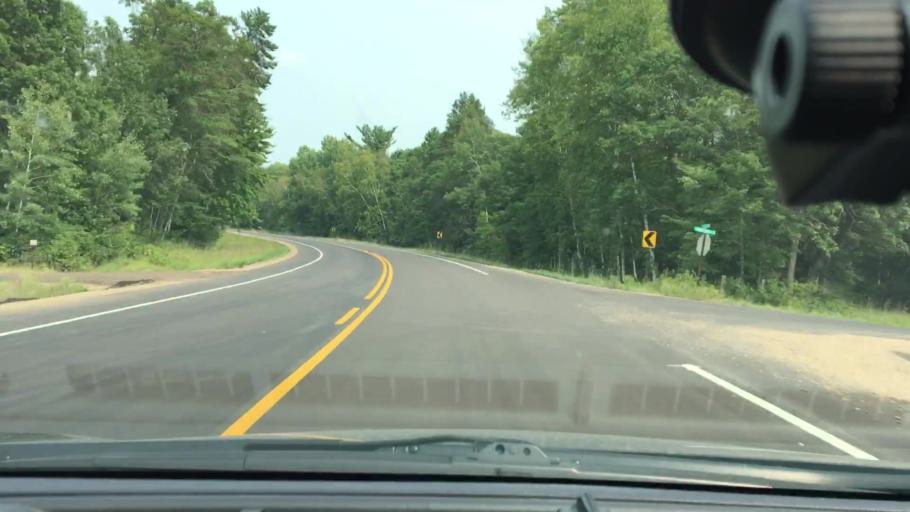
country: US
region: Minnesota
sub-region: Crow Wing County
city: Breezy Point
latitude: 46.5301
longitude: -94.2286
